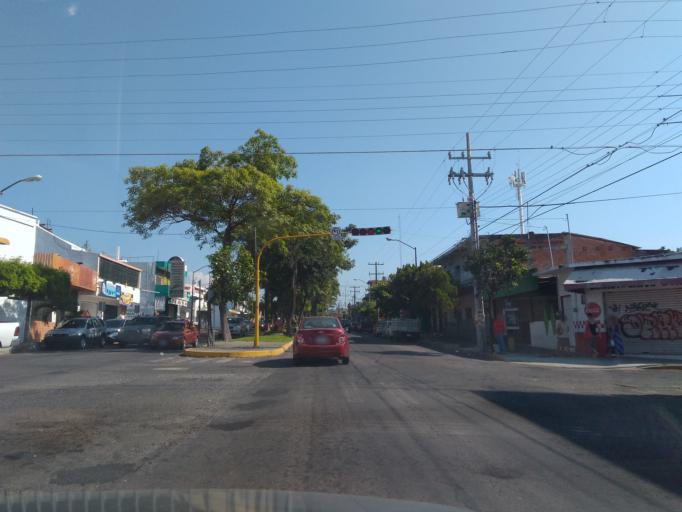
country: MX
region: Colima
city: Colima
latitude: 19.2490
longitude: -103.7328
